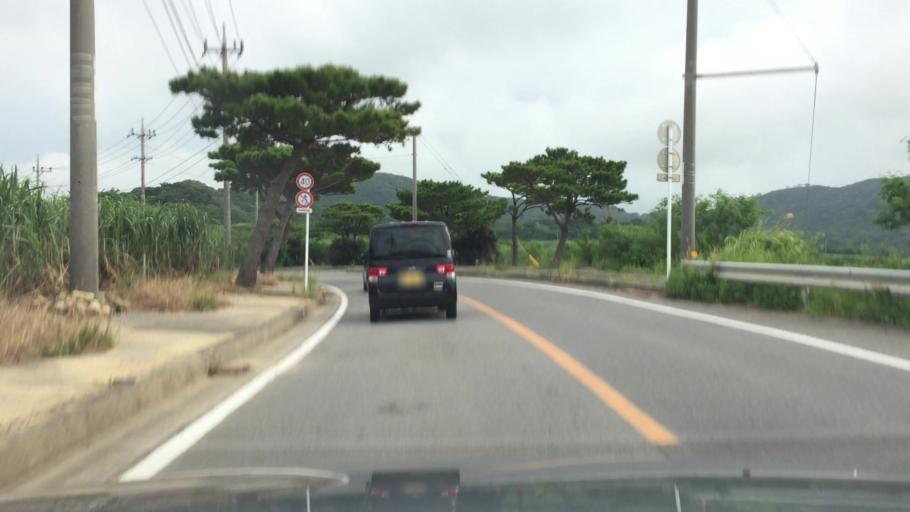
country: JP
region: Okinawa
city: Ishigaki
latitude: 24.3865
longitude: 124.1518
